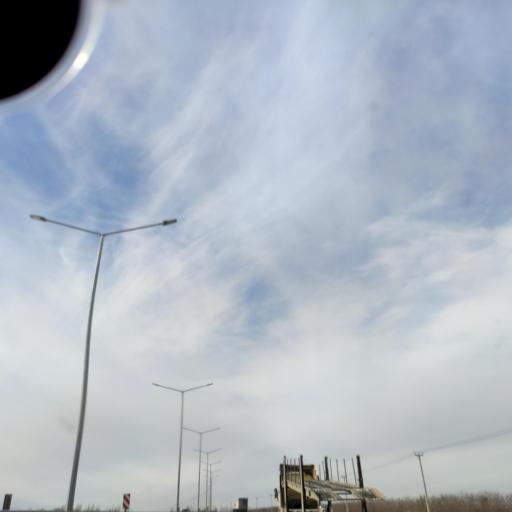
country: RU
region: Voronezj
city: Podkletnoye
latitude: 51.5843
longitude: 39.4548
